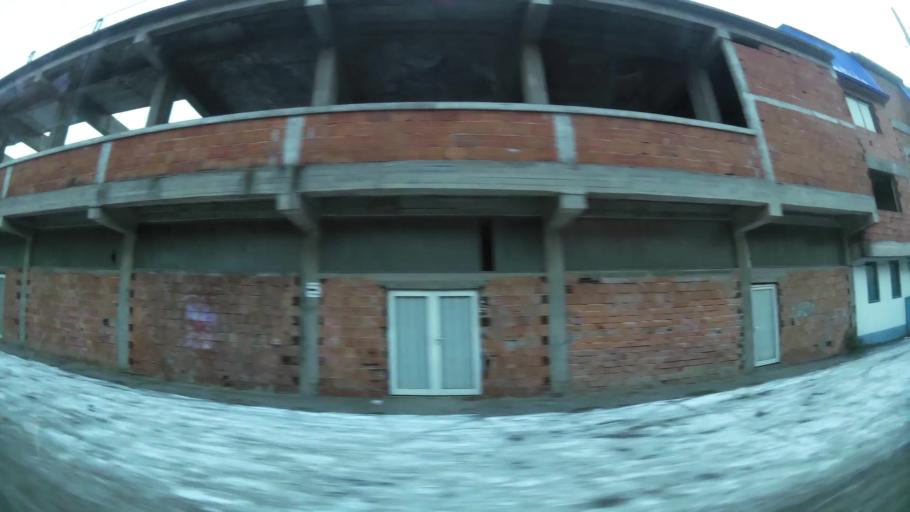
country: MK
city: Creshevo
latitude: 42.0013
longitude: 21.5031
